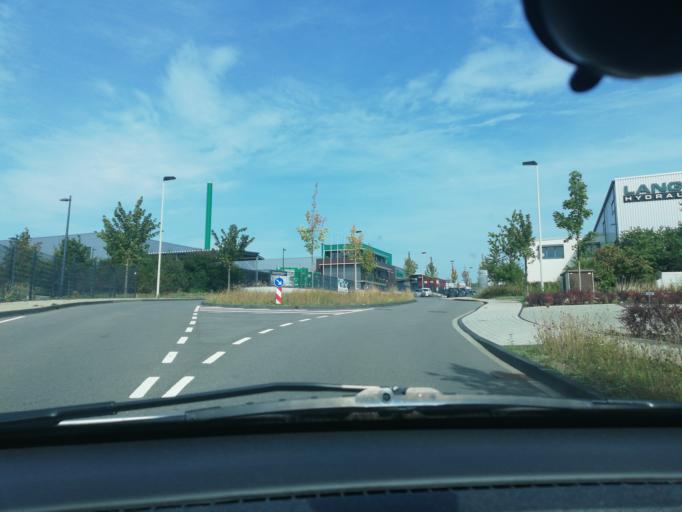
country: DE
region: North Rhine-Westphalia
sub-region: Regierungsbezirk Dusseldorf
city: Solingen
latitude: 51.2118
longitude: 7.0656
